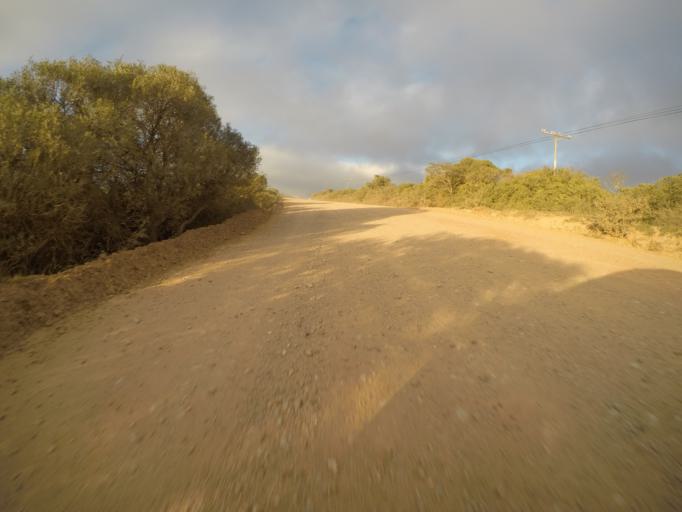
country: ZA
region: Western Cape
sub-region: Eden District Municipality
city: Mossel Bay
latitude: -34.1098
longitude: 22.0604
